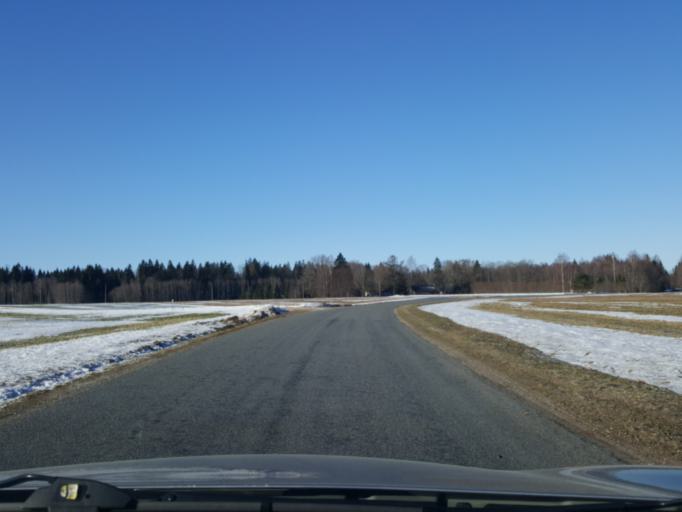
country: EE
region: Viljandimaa
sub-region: Suure-Jaani vald
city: Suure-Jaani
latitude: 58.5330
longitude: 25.5586
